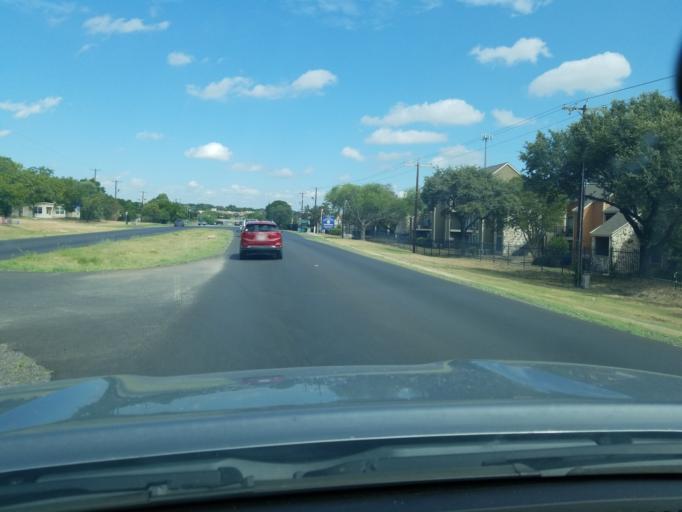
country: US
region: Texas
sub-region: Bexar County
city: Terrell Hills
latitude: 29.4893
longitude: -98.4306
